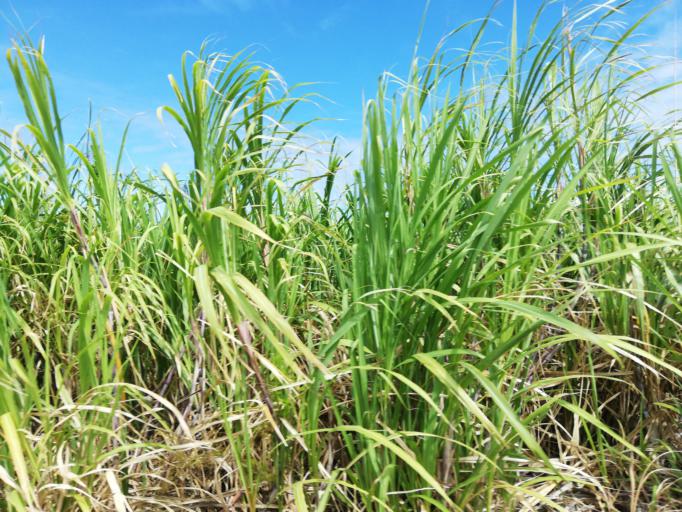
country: MU
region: Grand Port
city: Plaine Magnien
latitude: -20.4446
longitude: 57.6525
